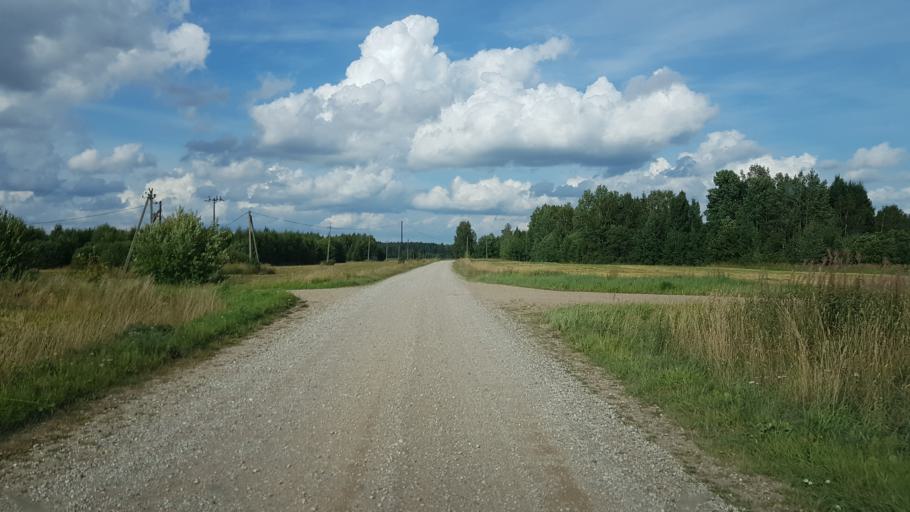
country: RU
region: Pskov
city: Pechory
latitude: 57.8047
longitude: 27.5074
